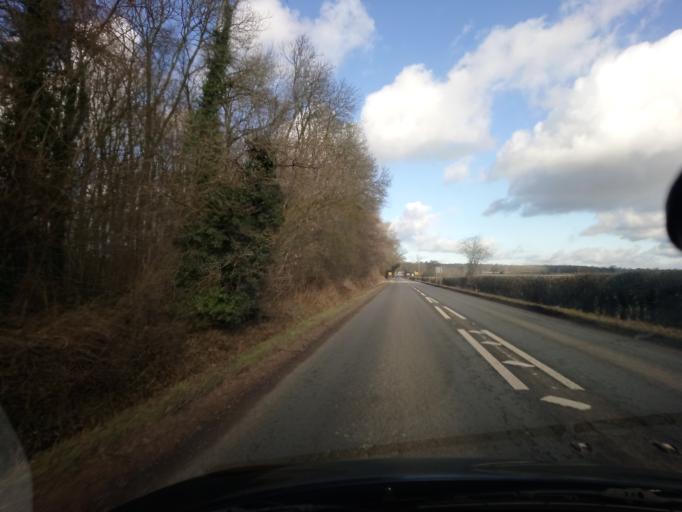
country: GB
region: England
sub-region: Shropshire
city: Clive
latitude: 52.7861
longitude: -2.7054
